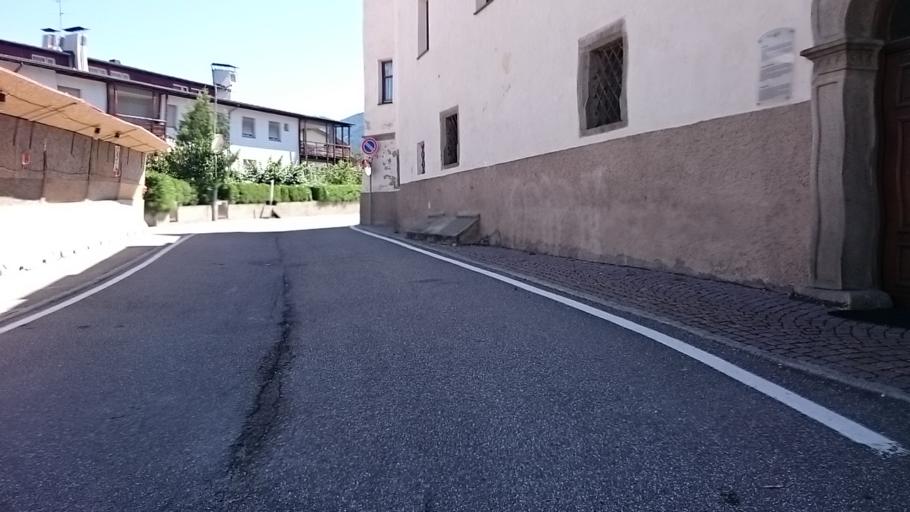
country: IT
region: Trentino-Alto Adige
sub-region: Bolzano
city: Brunico
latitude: 46.7937
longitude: 11.9430
